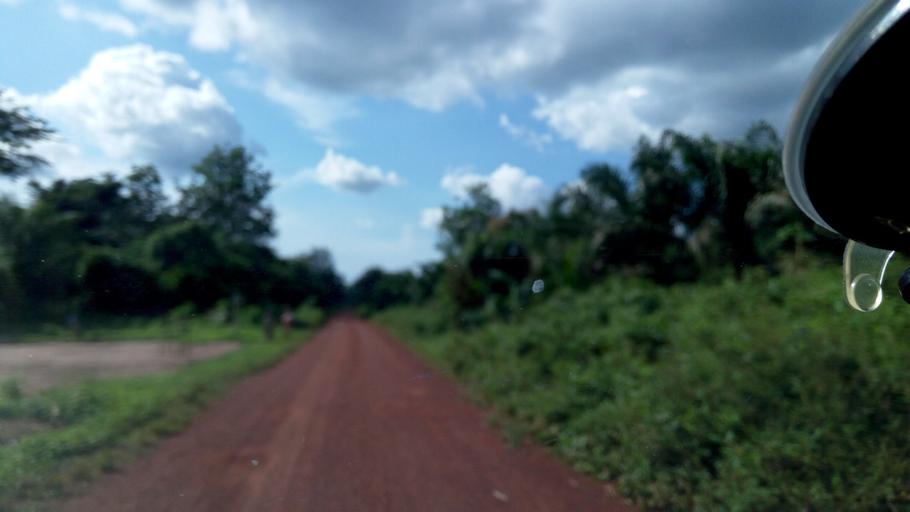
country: CD
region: Equateur
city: Libenge
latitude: 3.7674
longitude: 18.7075
